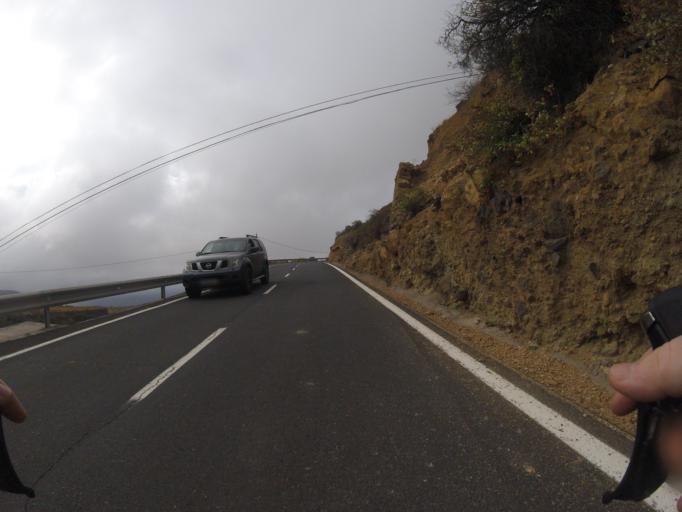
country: ES
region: Canary Islands
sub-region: Provincia de Santa Cruz de Tenerife
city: Fasnia
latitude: 28.2270
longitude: -16.4471
